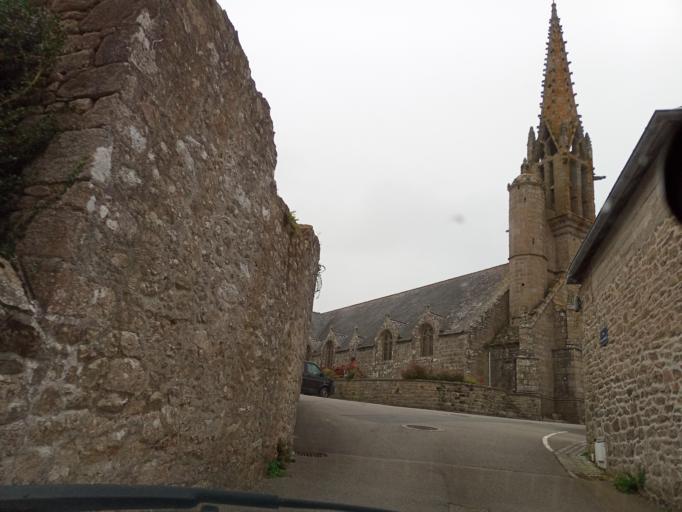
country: FR
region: Brittany
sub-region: Departement du Finistere
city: Esquibien
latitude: 48.0247
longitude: -4.5632
